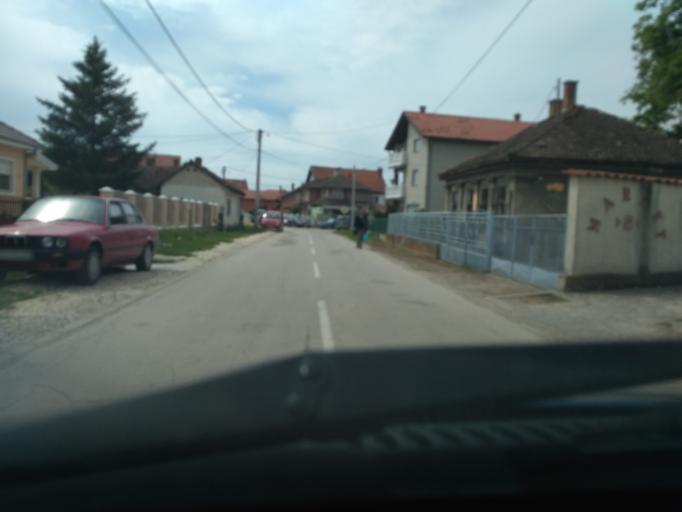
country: RS
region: Central Serbia
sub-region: Pomoravski Okrug
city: Svilajnac
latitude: 44.2350
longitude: 21.2018
